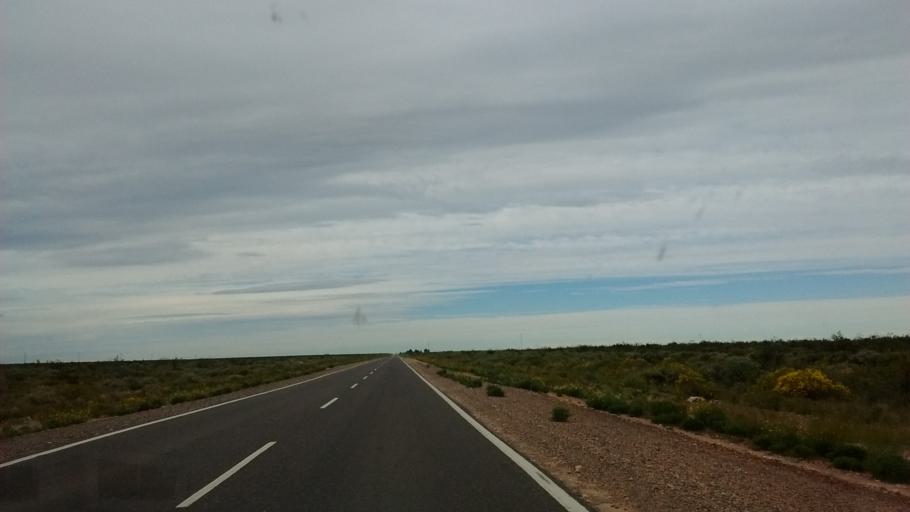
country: AR
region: Rio Negro
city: Contraalmirante Cordero
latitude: -38.3758
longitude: -68.0223
